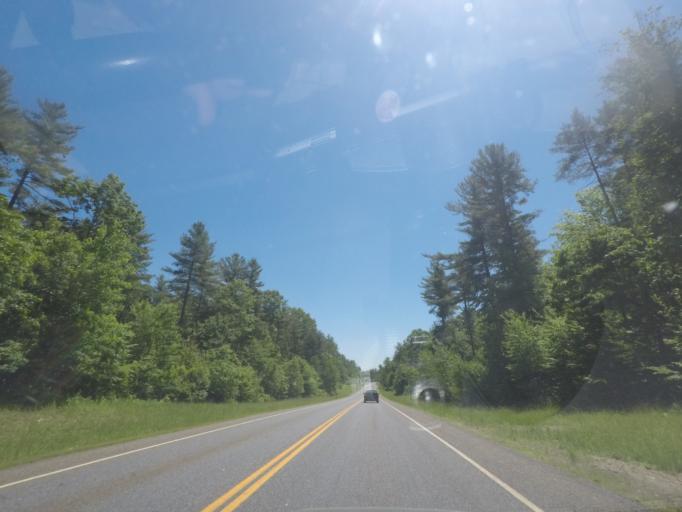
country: US
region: New York
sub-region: Saratoga County
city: Country Knolls
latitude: 42.9484
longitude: -73.7440
